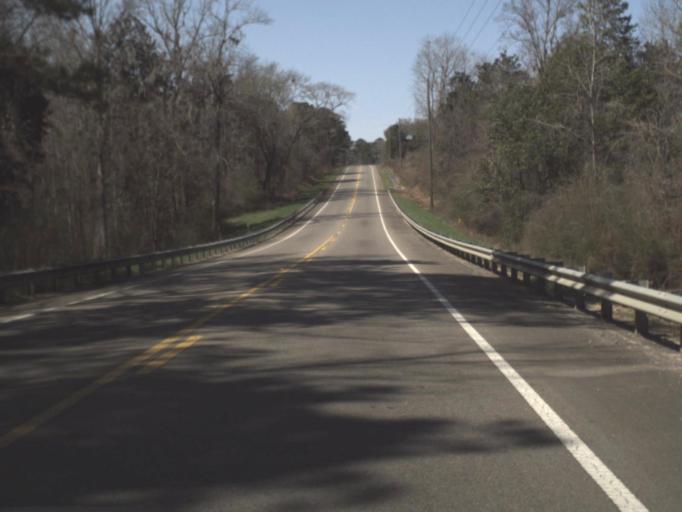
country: US
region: Florida
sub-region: Gadsden County
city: Gretna
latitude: 30.5924
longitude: -84.6590
